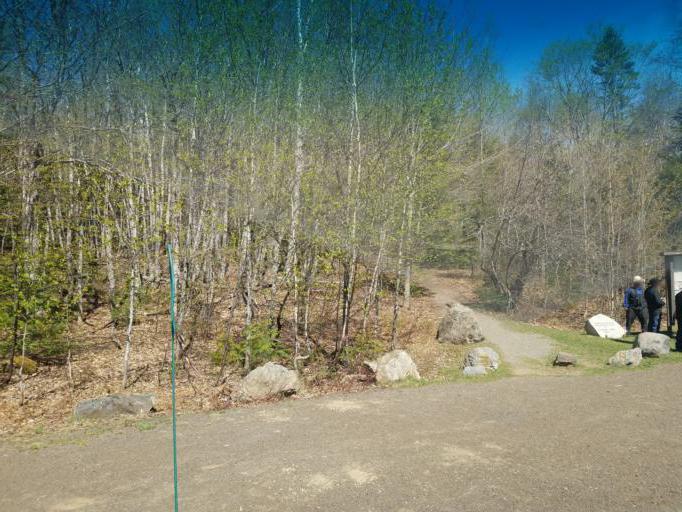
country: US
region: Maine
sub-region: Aroostook County
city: Presque Isle
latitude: 46.6649
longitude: -68.2292
